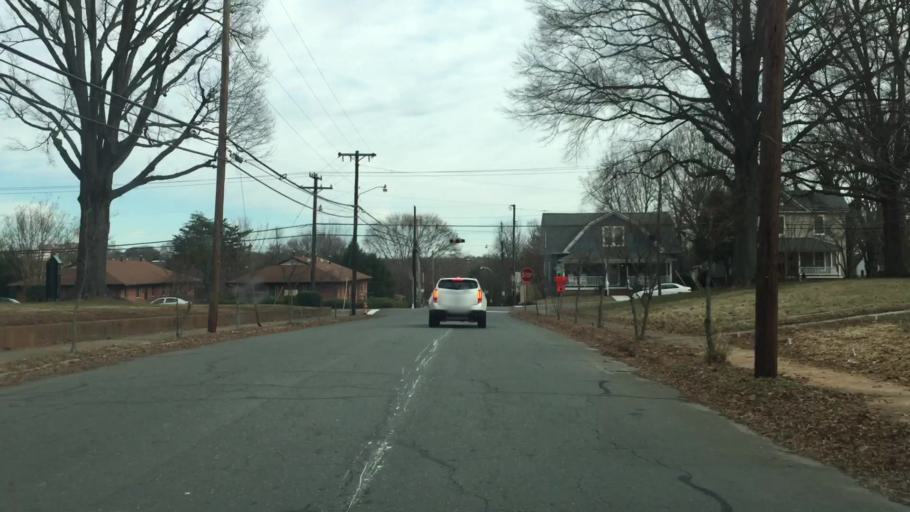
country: US
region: North Carolina
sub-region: Forsyth County
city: Winston-Salem
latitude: 36.0861
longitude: -80.2510
